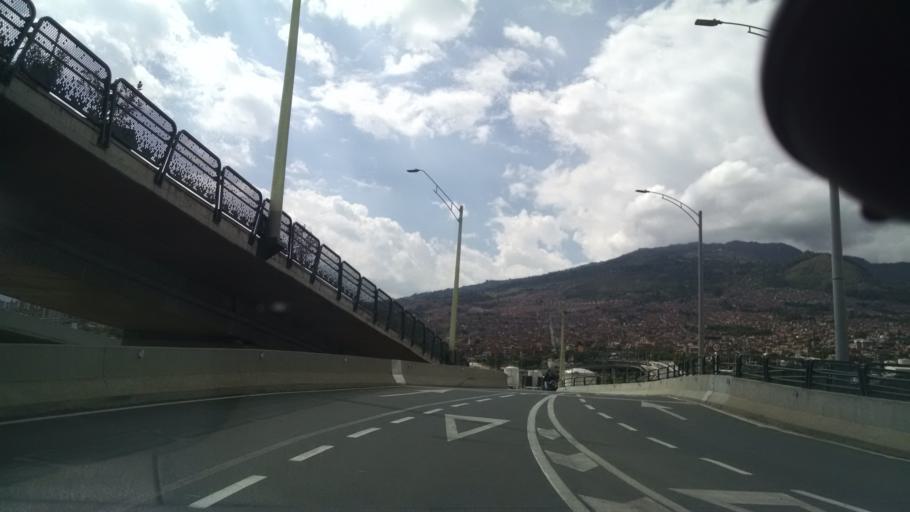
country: CO
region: Antioquia
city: Medellin
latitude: 6.2859
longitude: -75.5647
